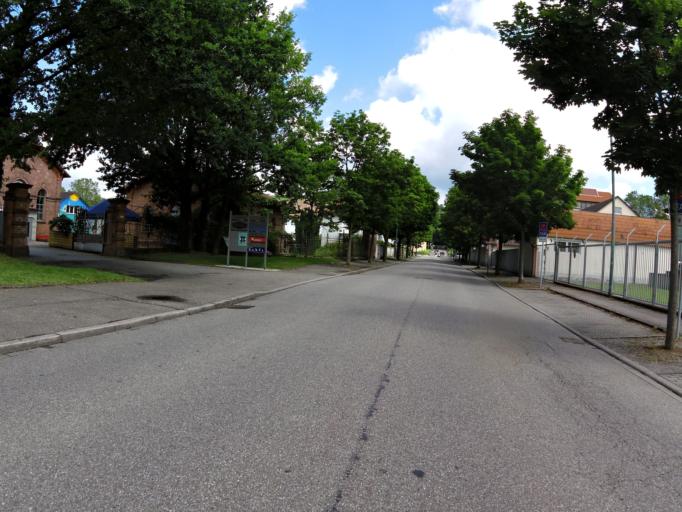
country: DE
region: Baden-Wuerttemberg
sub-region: Freiburg Region
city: Lahr
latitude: 48.3382
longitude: 7.8604
